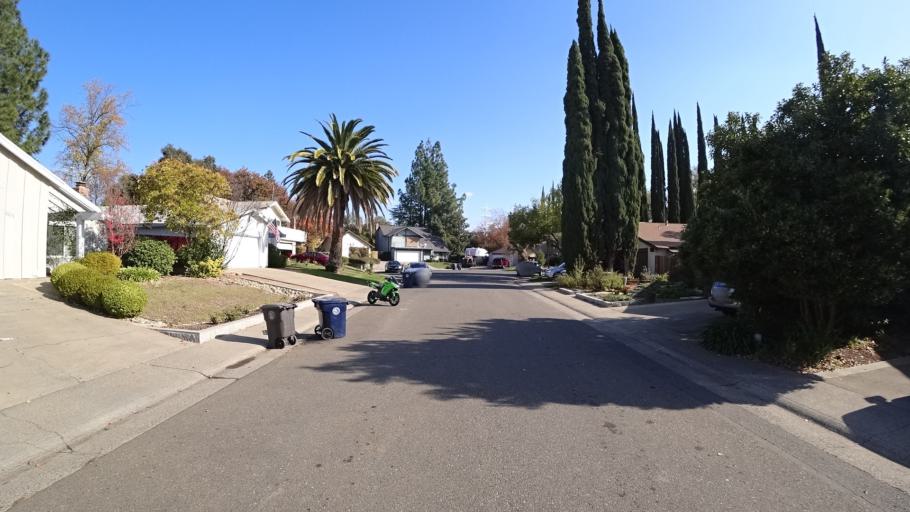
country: US
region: California
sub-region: Sacramento County
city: Citrus Heights
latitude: 38.6890
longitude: -121.2636
